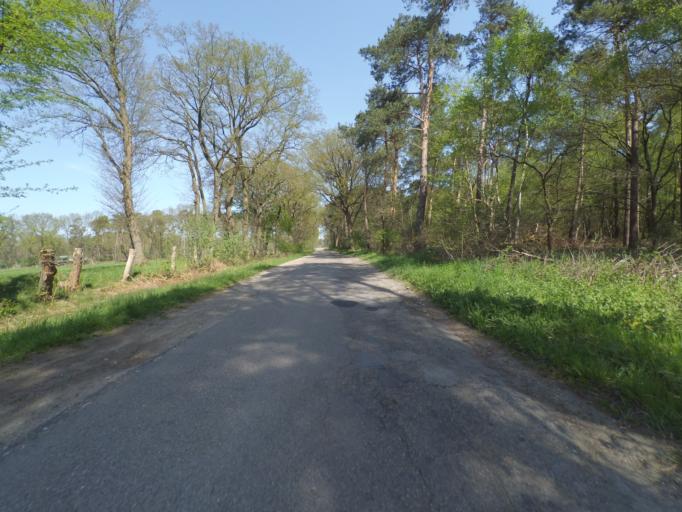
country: DE
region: North Rhine-Westphalia
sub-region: Regierungsbezirk Dusseldorf
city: Mehrhoog
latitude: 51.7244
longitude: 6.5304
